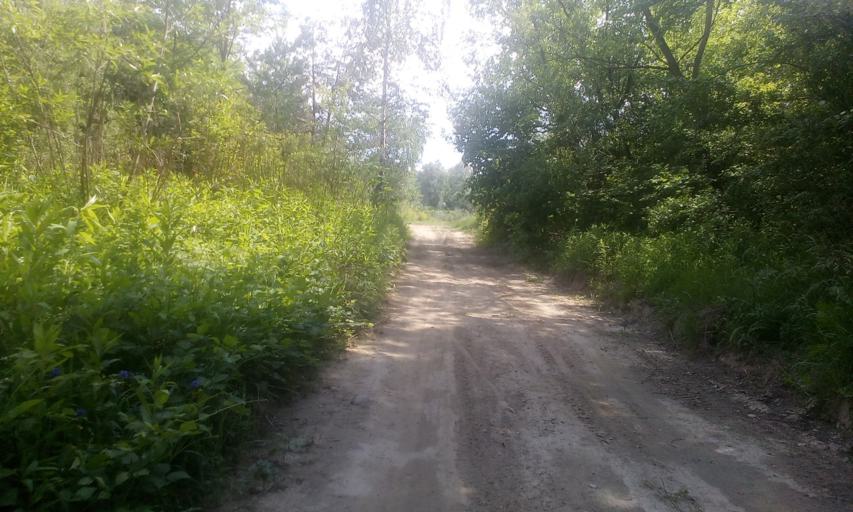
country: PL
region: Lesser Poland Voivodeship
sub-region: Powiat nowosadecki
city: Stary Sacz
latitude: 49.5734
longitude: 20.6556
